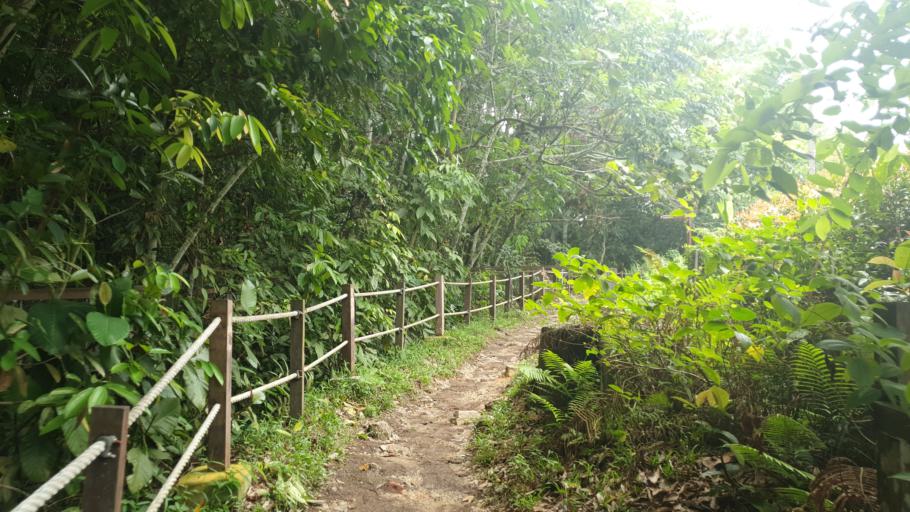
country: SG
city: Singapore
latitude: 1.3571
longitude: 103.8190
